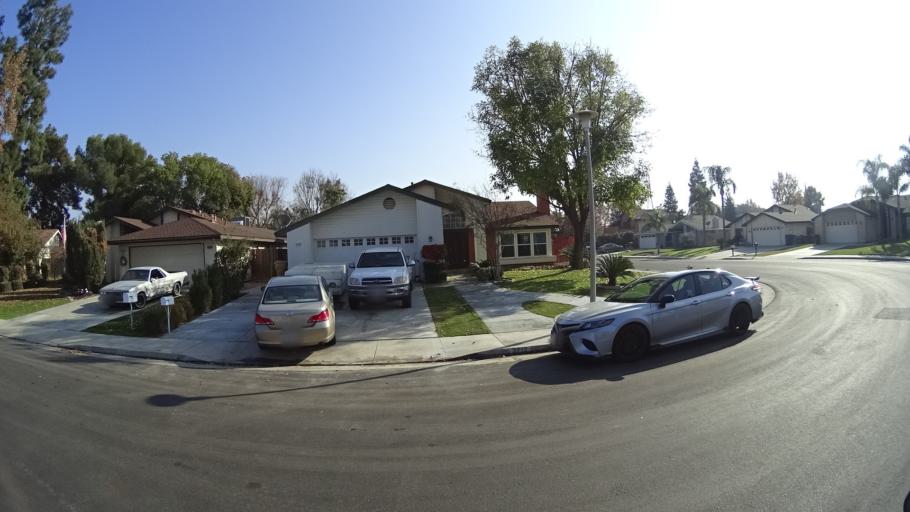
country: US
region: California
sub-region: Kern County
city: Greenacres
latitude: 35.3202
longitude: -119.0877
